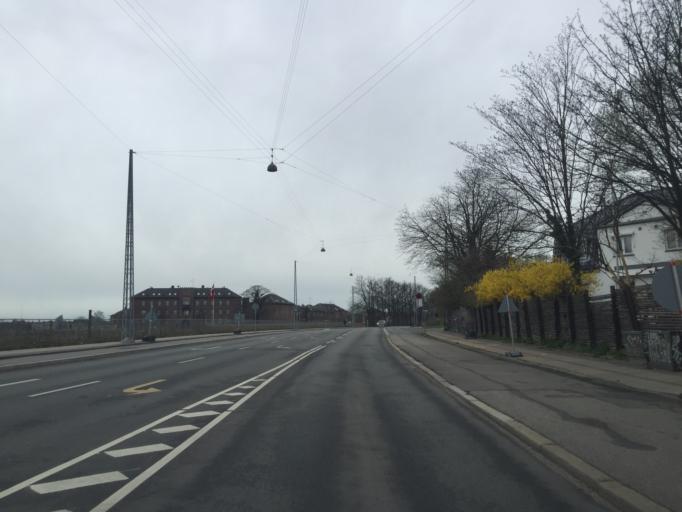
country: DK
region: Capital Region
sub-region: Gentofte Kommune
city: Charlottenlund
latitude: 55.7169
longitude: 12.5766
